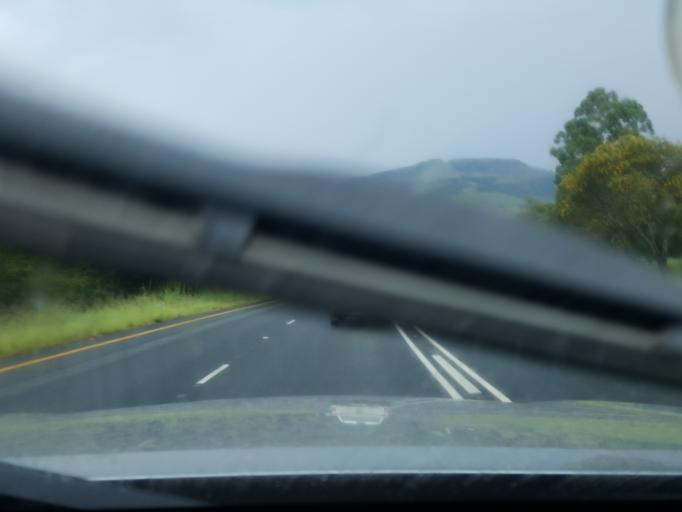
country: ZA
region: Mpumalanga
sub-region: Nkangala District Municipality
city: Belfast
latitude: -25.6243
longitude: 30.3984
